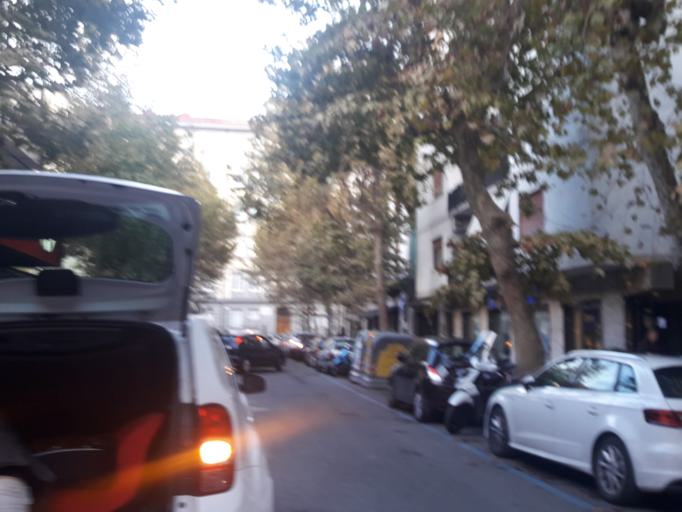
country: IT
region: Campania
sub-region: Provincia di Napoli
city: Napoli
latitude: 40.8436
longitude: 14.2339
